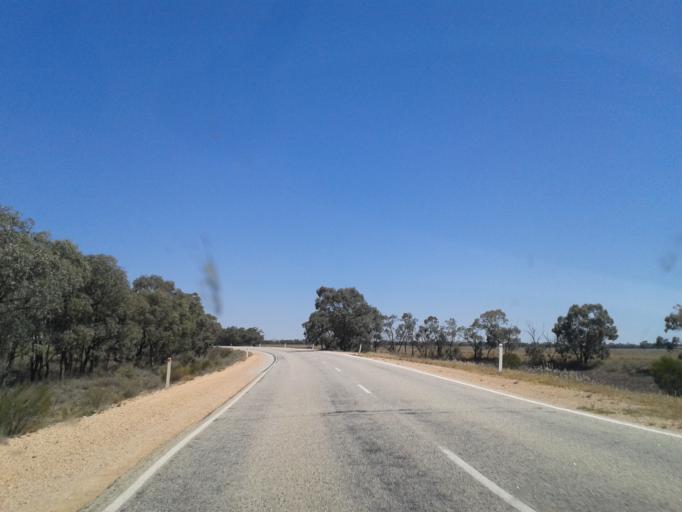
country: AU
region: Victoria
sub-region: Swan Hill
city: Swan Hill
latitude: -34.9360
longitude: 143.3007
